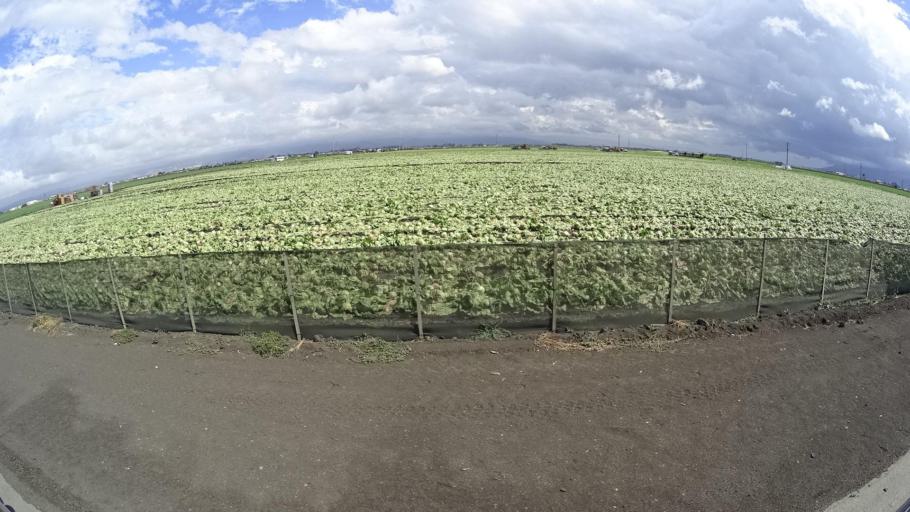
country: US
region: California
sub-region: Monterey County
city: Boronda
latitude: 36.6855
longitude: -121.7066
